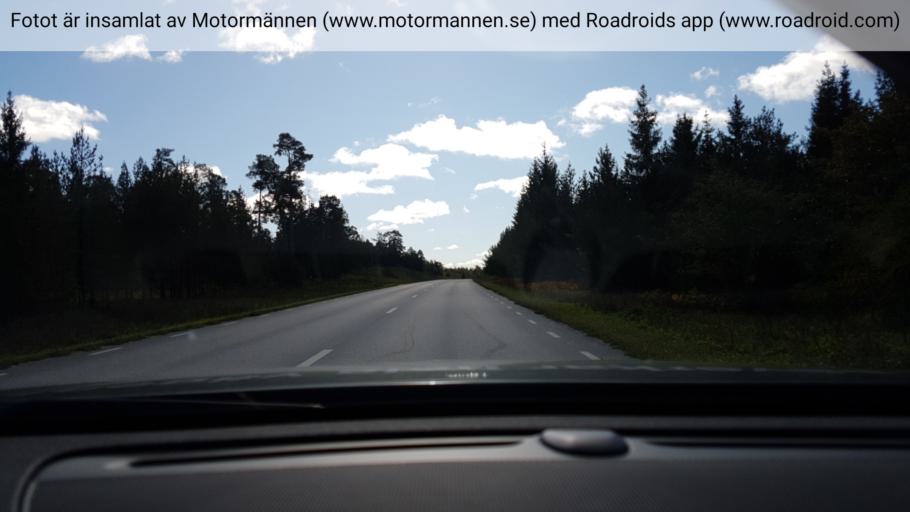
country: SE
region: Gotland
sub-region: Gotland
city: Slite
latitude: 57.7399
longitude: 18.7904
